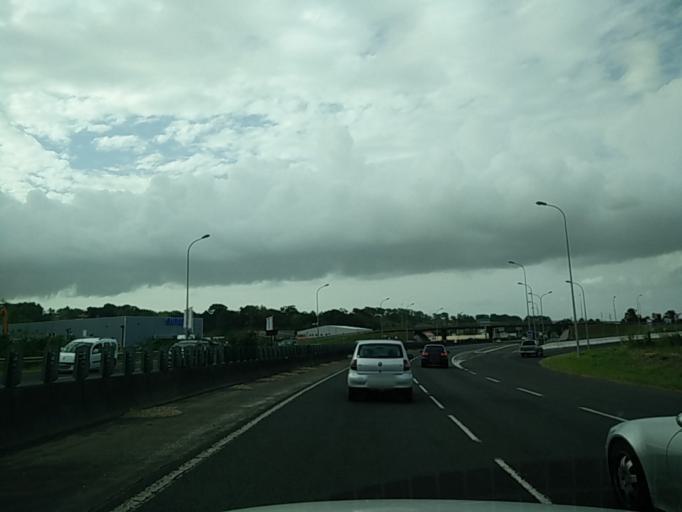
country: GP
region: Guadeloupe
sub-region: Guadeloupe
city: Petit-Bourg
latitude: 16.2004
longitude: -61.6061
